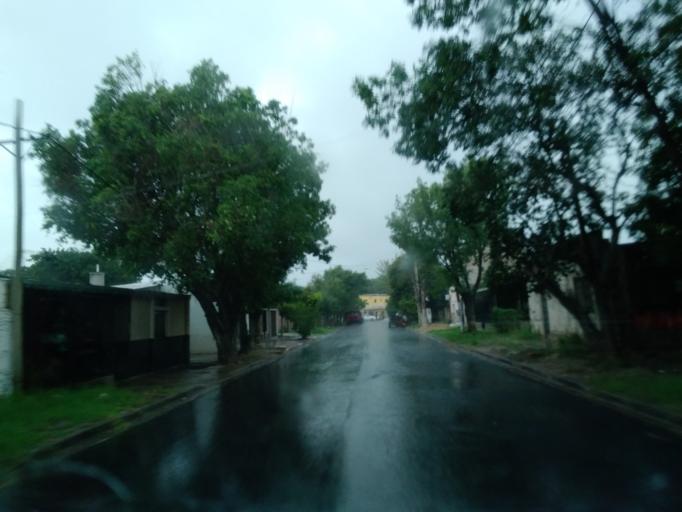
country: AR
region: Corrientes
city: Corrientes
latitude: -27.4908
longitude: -58.8222
